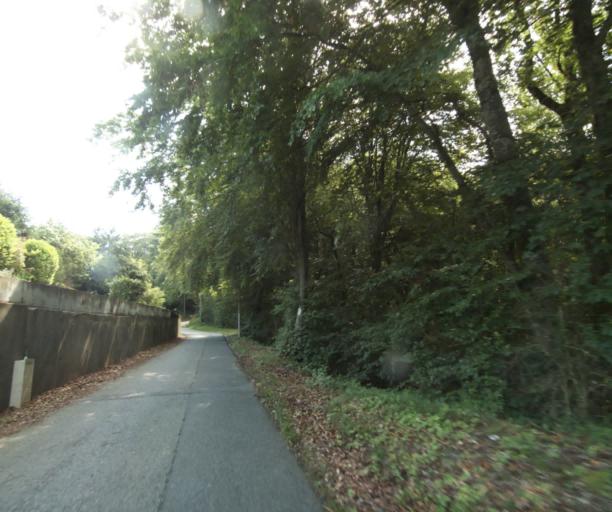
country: FR
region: Rhone-Alpes
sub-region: Departement de la Haute-Savoie
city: Thonon-les-Bains
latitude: 46.3583
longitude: 6.4986
